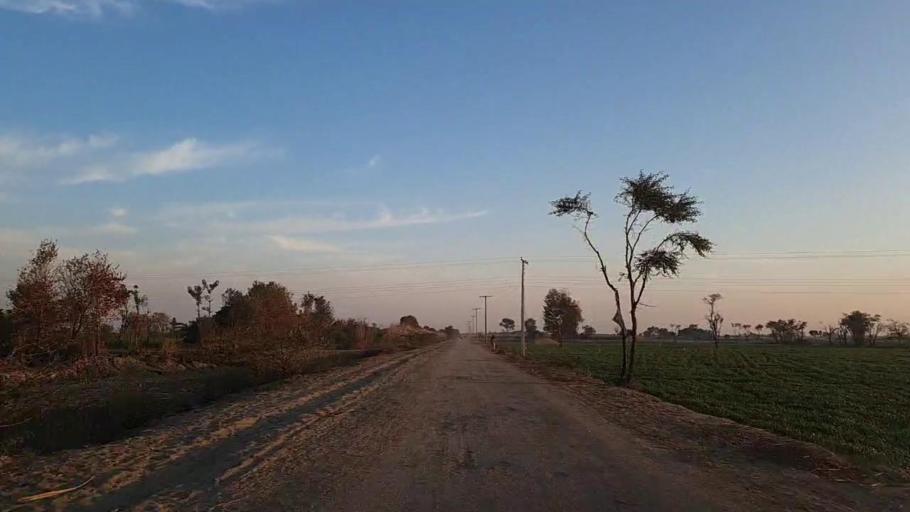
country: PK
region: Sindh
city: Bandhi
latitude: 26.6250
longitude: 68.3717
